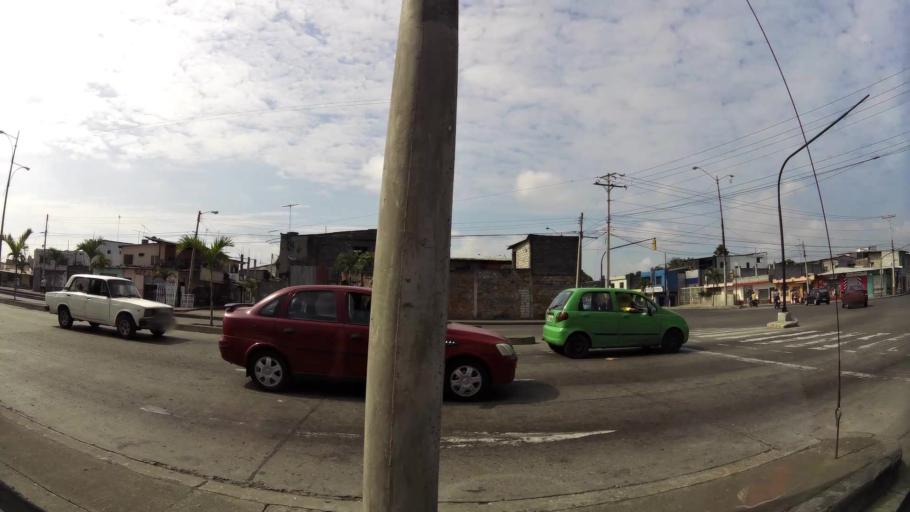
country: EC
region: Guayas
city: Guayaquil
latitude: -2.2615
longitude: -79.8916
